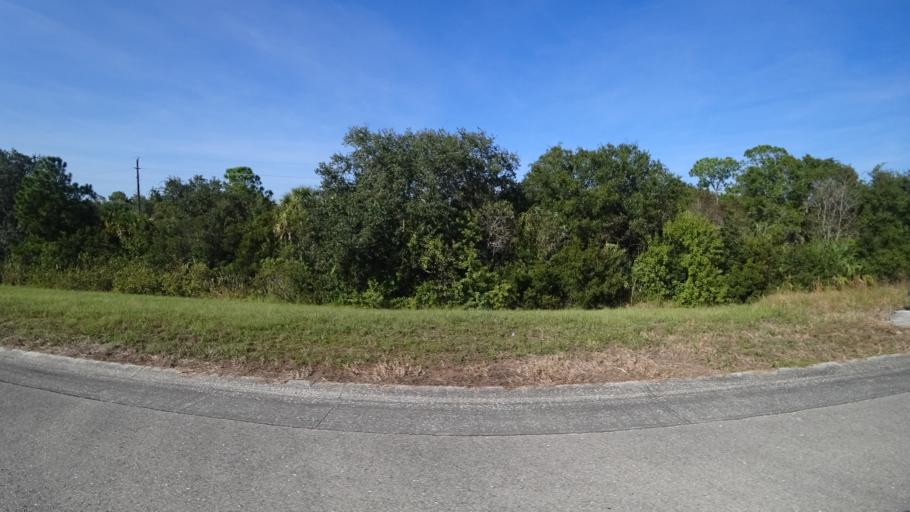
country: US
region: Florida
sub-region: Sarasota County
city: Desoto Lakes
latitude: 27.4179
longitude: -82.4587
